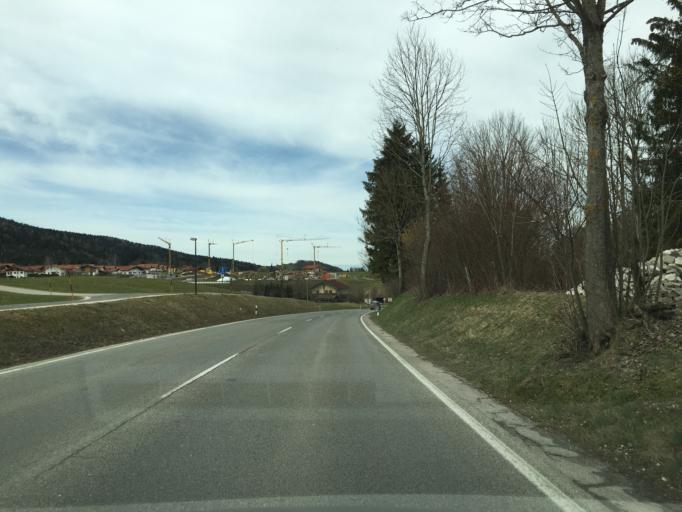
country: DE
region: Bavaria
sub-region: Upper Bavaria
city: Inzell
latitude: 47.7823
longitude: 12.7341
